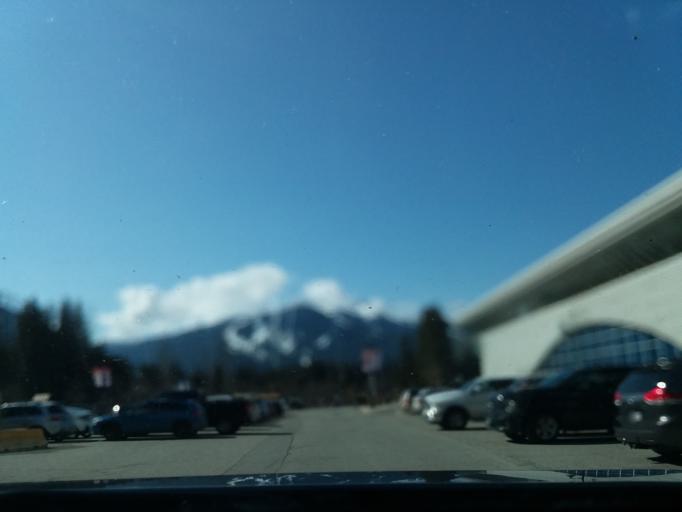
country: CA
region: British Columbia
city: Whistler
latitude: 50.1452
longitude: -122.9601
